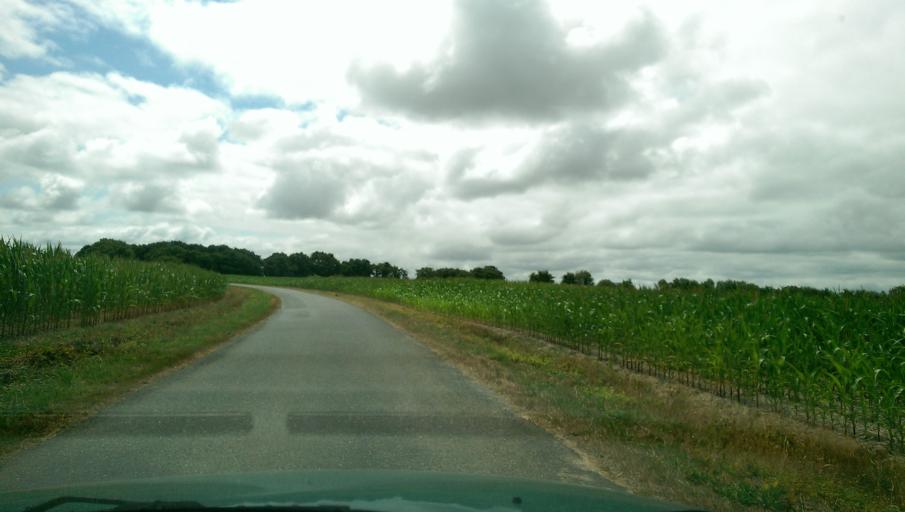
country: FR
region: Pays de la Loire
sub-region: Departement de la Loire-Atlantique
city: Remouille
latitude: 47.0726
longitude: -1.3655
